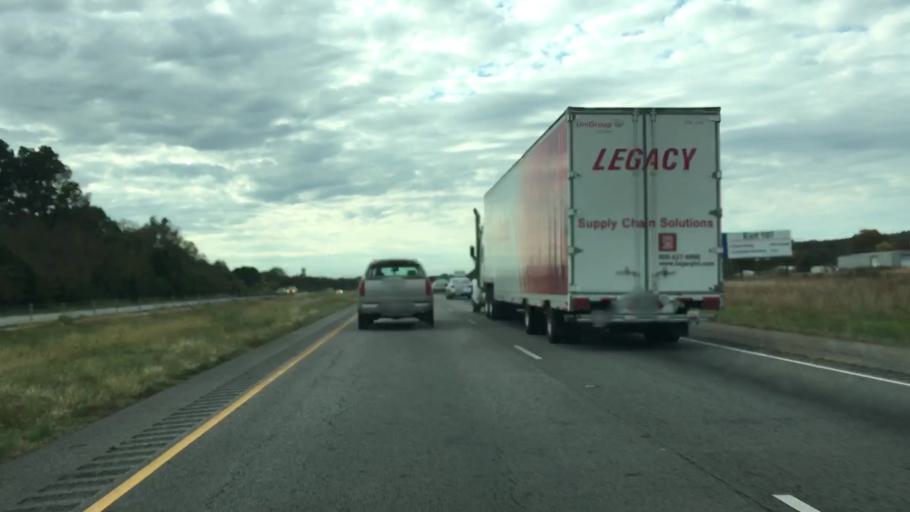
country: US
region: Arkansas
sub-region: Conway County
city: Morrilton
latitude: 35.1632
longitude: -92.6348
